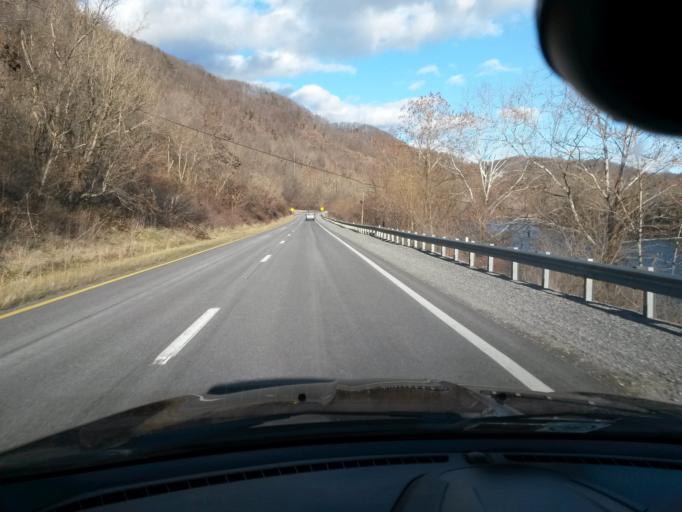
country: US
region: Virginia
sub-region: Giles County
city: Narrows
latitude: 37.3852
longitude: -80.8416
